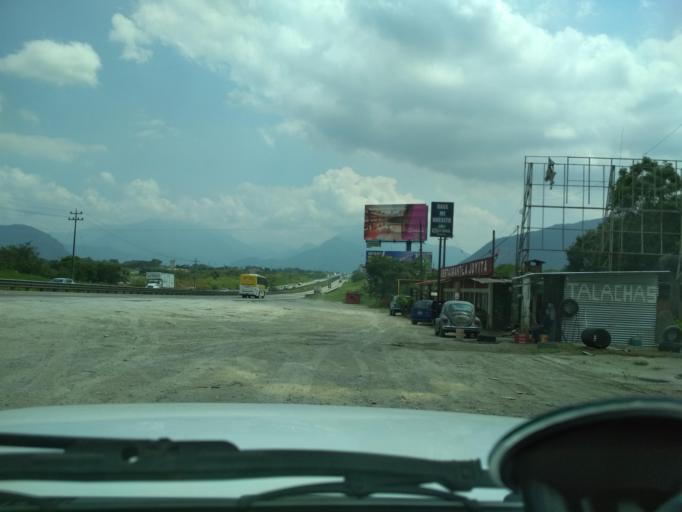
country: MX
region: Veracruz
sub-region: Ixtaczoquitlan
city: Buenavista
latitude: 18.8875
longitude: -97.0485
